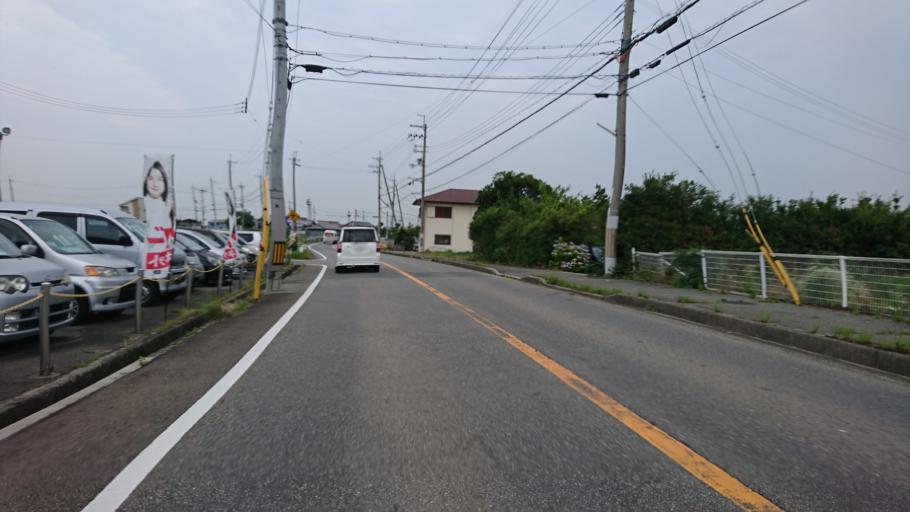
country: JP
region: Hyogo
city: Miki
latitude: 34.7380
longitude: 134.9669
